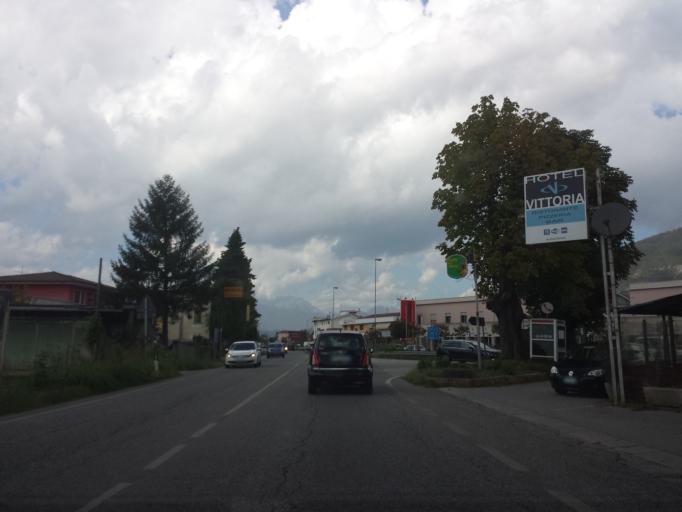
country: IT
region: Veneto
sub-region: Provincia di Vicenza
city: Cereda-Cozza Cornedo
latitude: 45.5968
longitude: 11.3700
